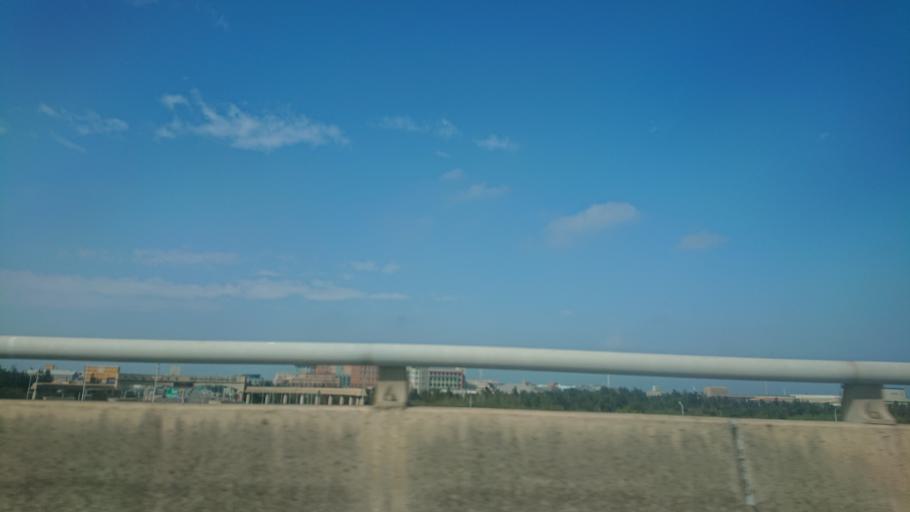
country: TW
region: Taiwan
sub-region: Changhua
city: Chang-hua
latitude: 24.0775
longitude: 120.4171
